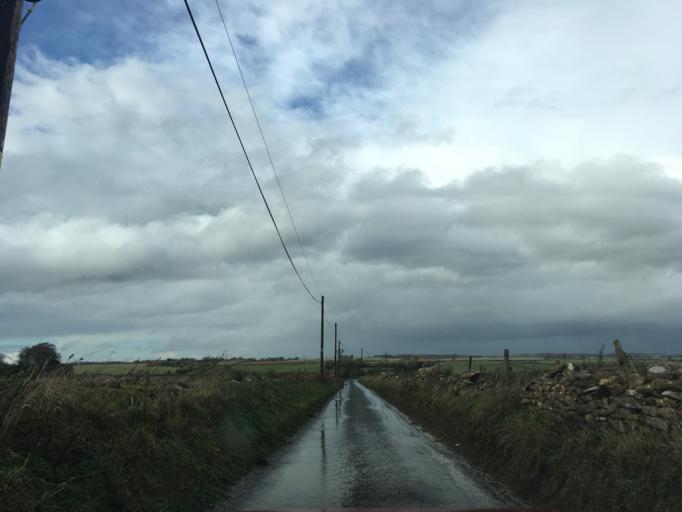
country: GB
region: England
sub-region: South Gloucestershire
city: Marshfield
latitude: 51.4666
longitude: -2.3247
